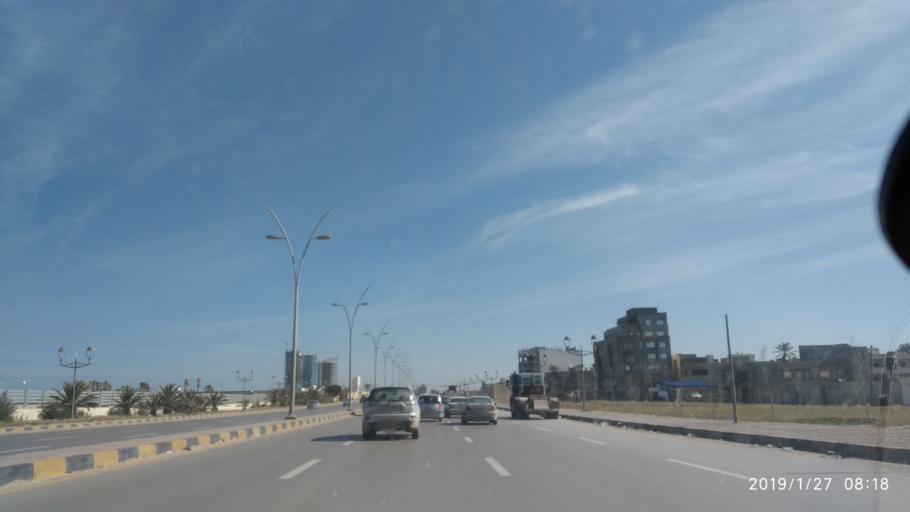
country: LY
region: Tripoli
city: Tripoli
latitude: 32.9068
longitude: 13.2510
